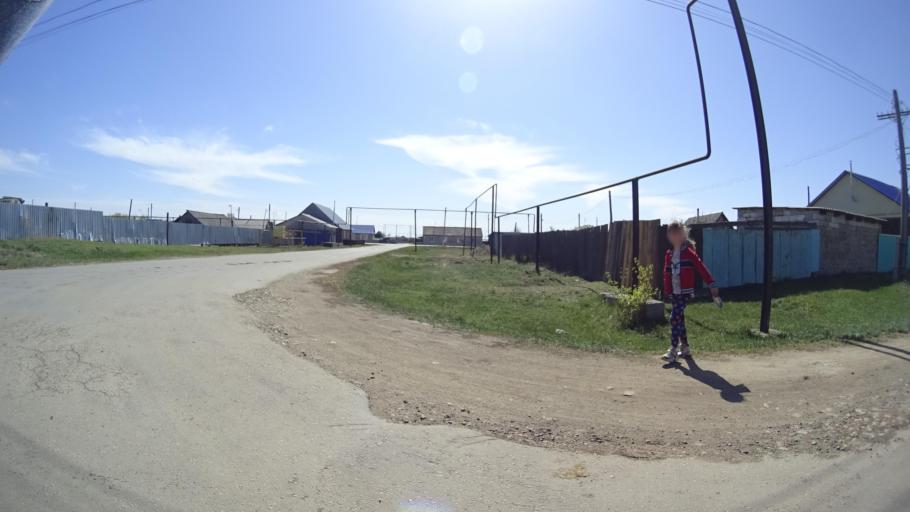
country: RU
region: Chelyabinsk
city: Chesma
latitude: 53.7949
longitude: 61.0345
